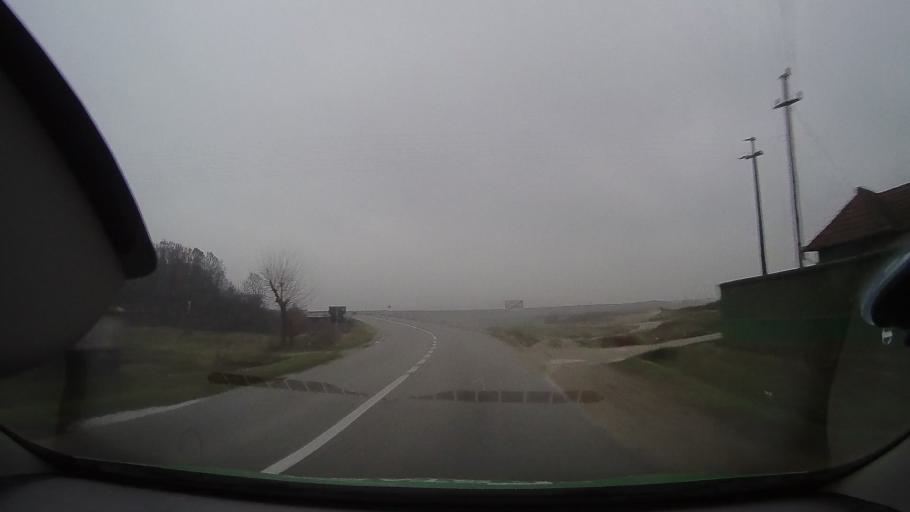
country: RO
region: Bihor
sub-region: Comuna Tinca
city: Gurbediu
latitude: 46.7838
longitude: 21.8674
